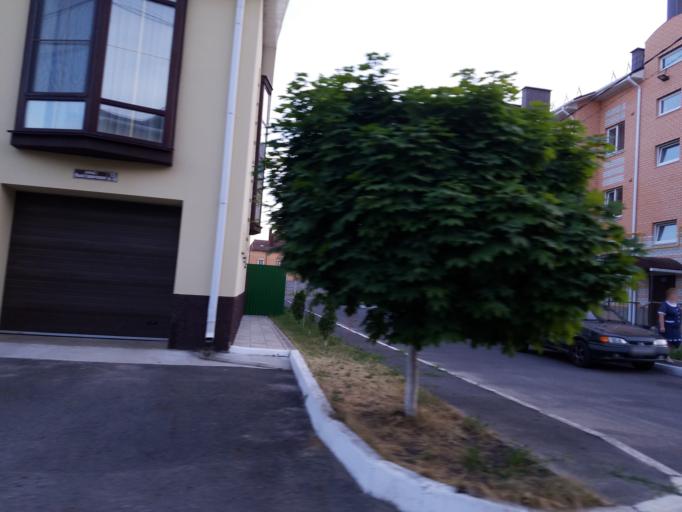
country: RU
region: Orjol
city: Znamenka
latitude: 52.9123
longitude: 36.0064
